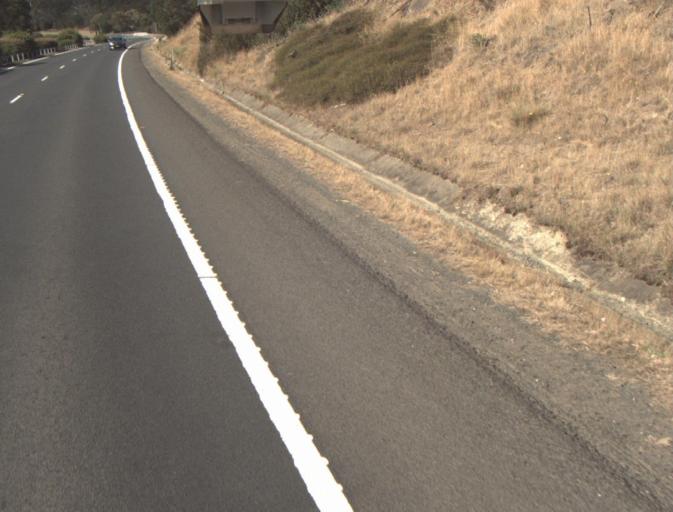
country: AU
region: Tasmania
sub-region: Launceston
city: Summerhill
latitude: -41.4811
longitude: 147.1495
